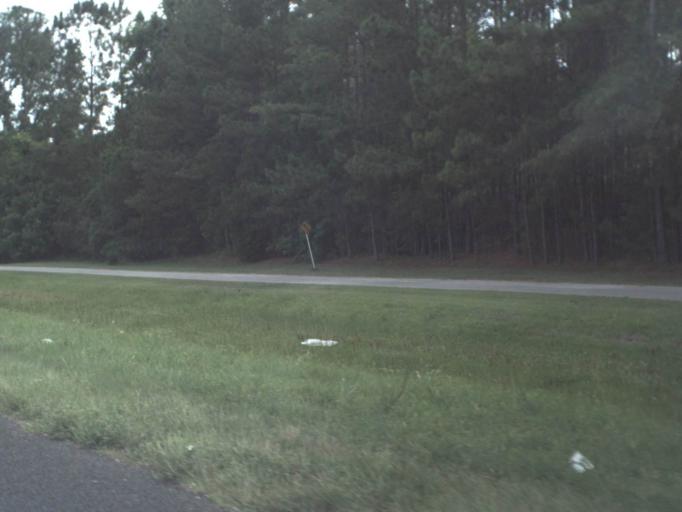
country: US
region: Florida
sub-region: Clay County
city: Orange Park
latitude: 30.1102
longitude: -81.7053
